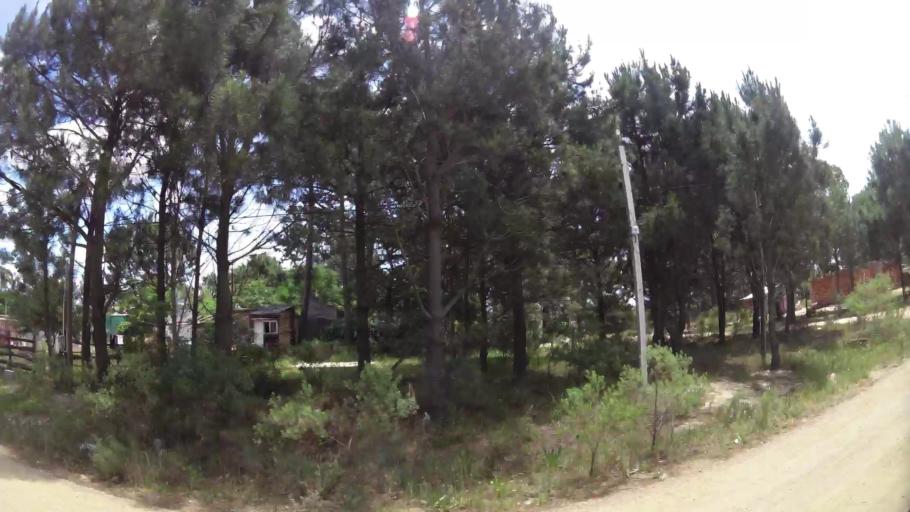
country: UY
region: Canelones
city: Pando
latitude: -34.8045
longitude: -55.9413
